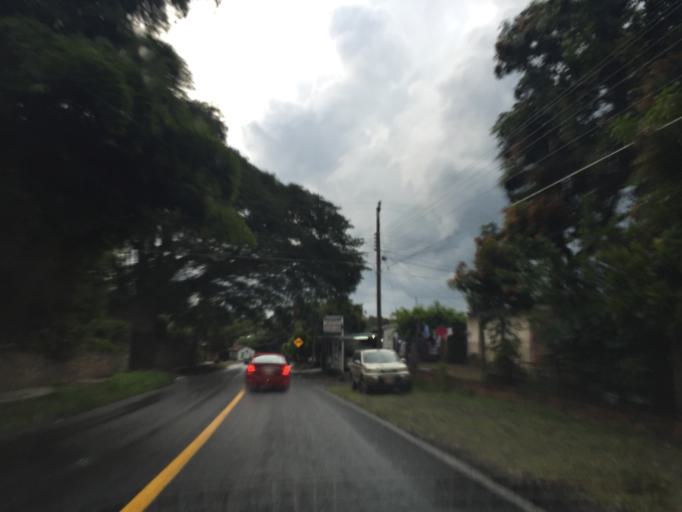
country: MX
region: Colima
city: Queseria
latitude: 19.3657
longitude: -103.5789
